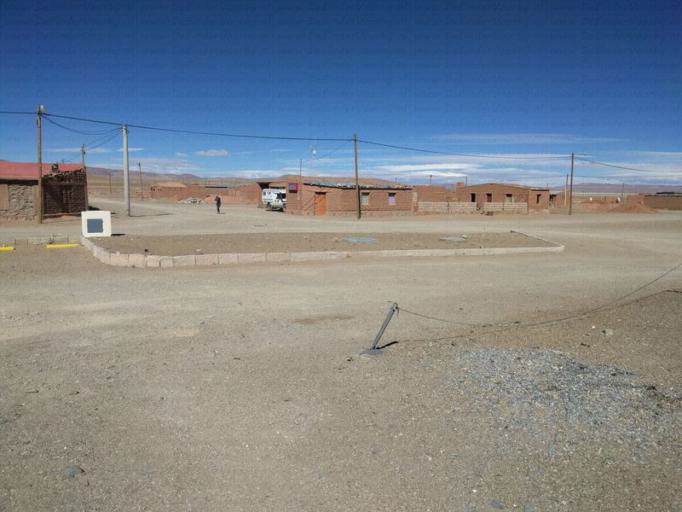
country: AR
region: Jujuy
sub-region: Departamento de Susques
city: Susques
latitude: -23.2383
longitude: -67.0189
